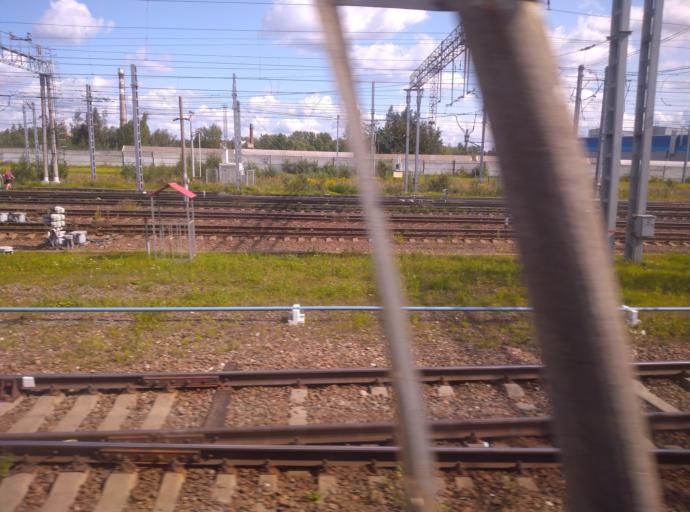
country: RU
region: St.-Petersburg
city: Obukhovo
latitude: 59.8508
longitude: 30.4513
